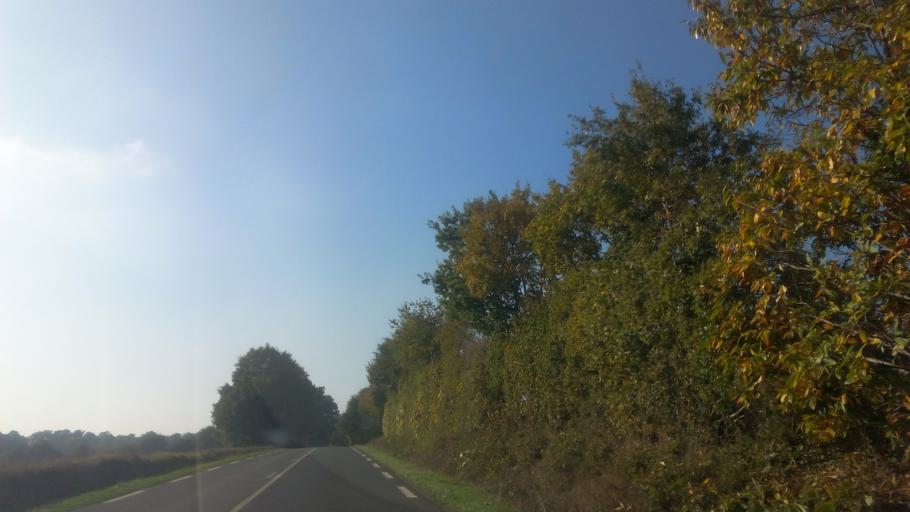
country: FR
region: Pays de la Loire
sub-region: Departement de la Loire-Atlantique
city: Avessac
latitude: 47.6397
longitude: -2.0040
